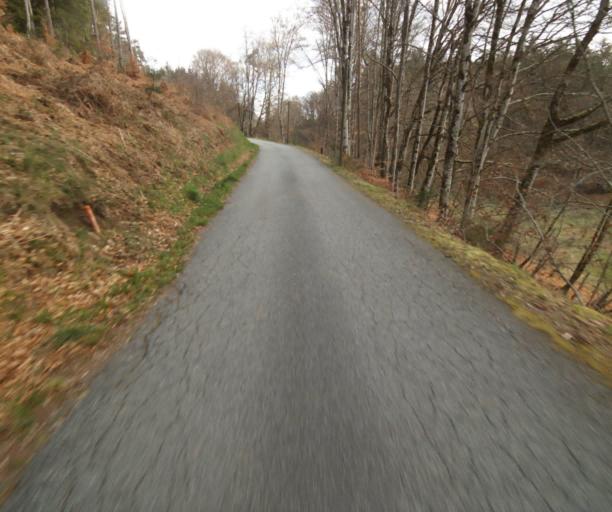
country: FR
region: Limousin
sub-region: Departement de la Correze
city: Correze
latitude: 45.3844
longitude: 1.8773
